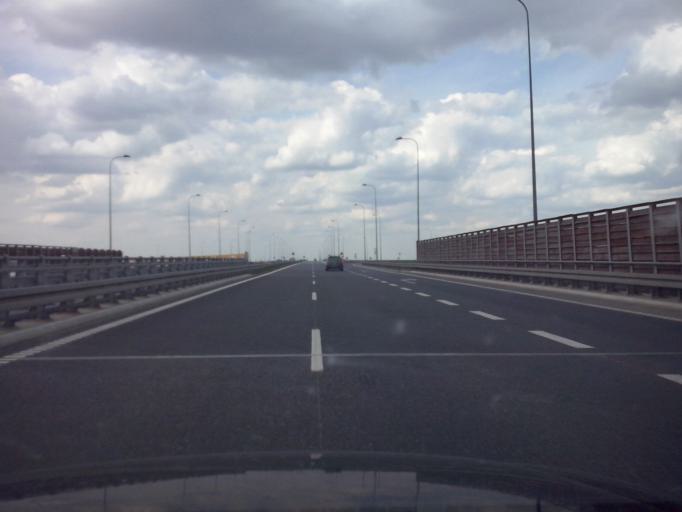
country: PL
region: Subcarpathian Voivodeship
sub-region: Powiat rzeszowski
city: Trzebownisko
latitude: 50.0861
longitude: 22.0613
